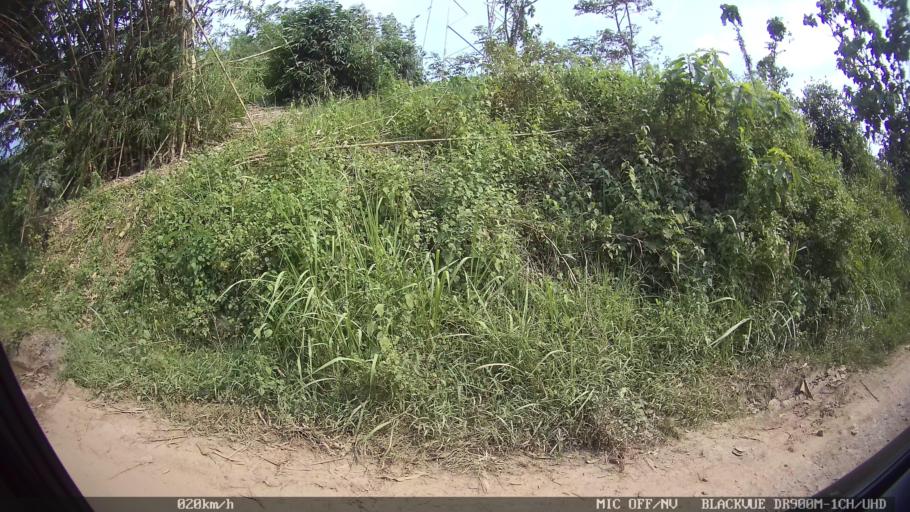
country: ID
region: Lampung
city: Kedondong
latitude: -5.4102
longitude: 105.0135
